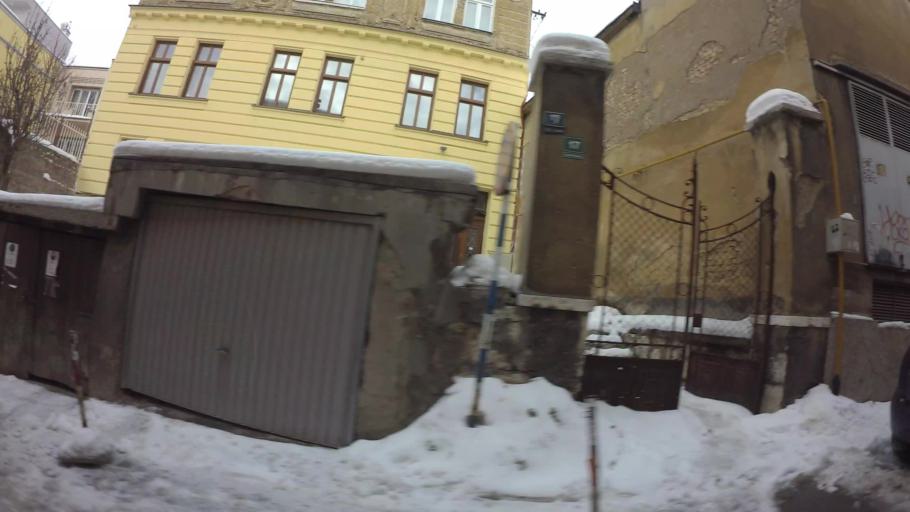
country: BA
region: Federation of Bosnia and Herzegovina
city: Kobilja Glava
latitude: 43.8611
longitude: 18.4270
